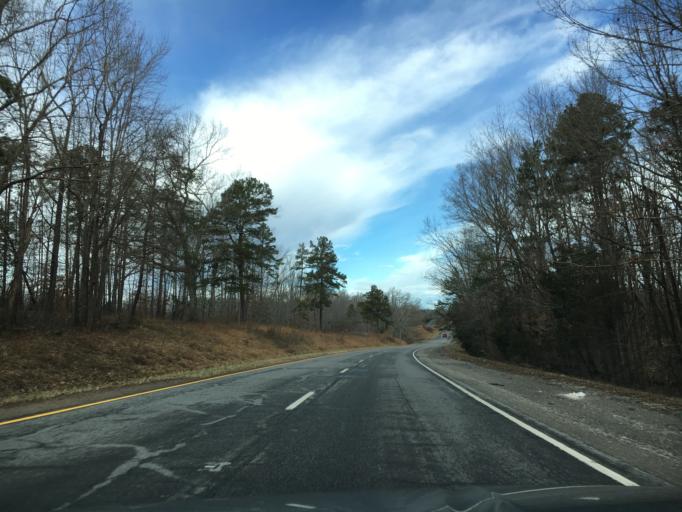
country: US
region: Virginia
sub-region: Nottoway County
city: Crewe
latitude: 37.2009
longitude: -78.2269
